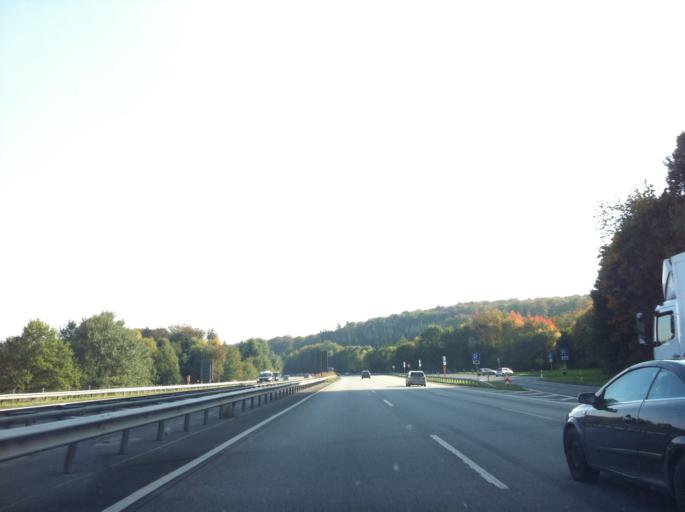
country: DE
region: Rheinland-Pfalz
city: Oberhaid
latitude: 50.5058
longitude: 7.7160
